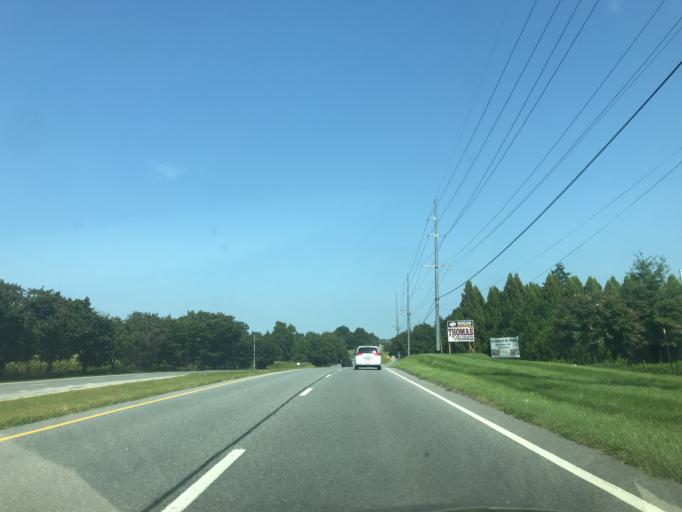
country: US
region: Maryland
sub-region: Calvert County
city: Dunkirk Town Center
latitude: 38.6848
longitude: -76.6354
